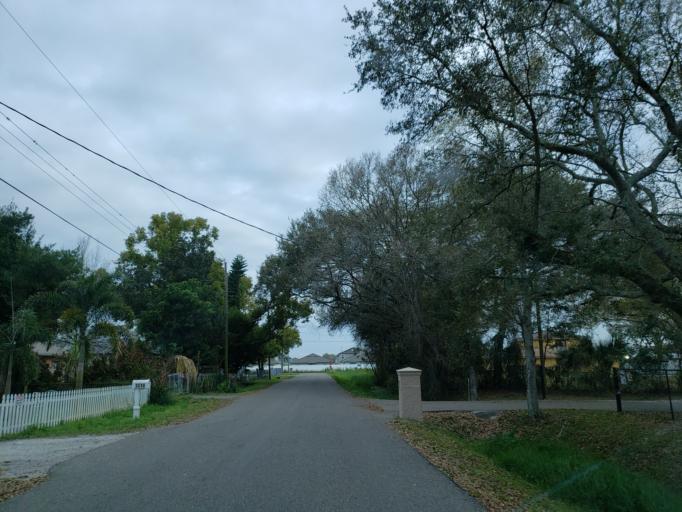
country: US
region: Florida
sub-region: Hillsborough County
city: Palm River-Clair Mel
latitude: 27.9166
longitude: -82.3728
